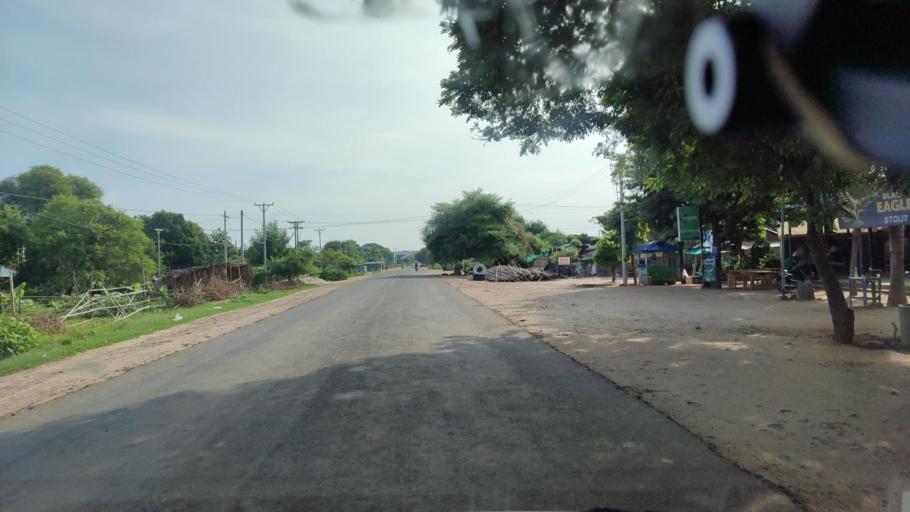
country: MM
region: Magway
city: Pakokku
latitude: 21.2666
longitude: 95.0554
